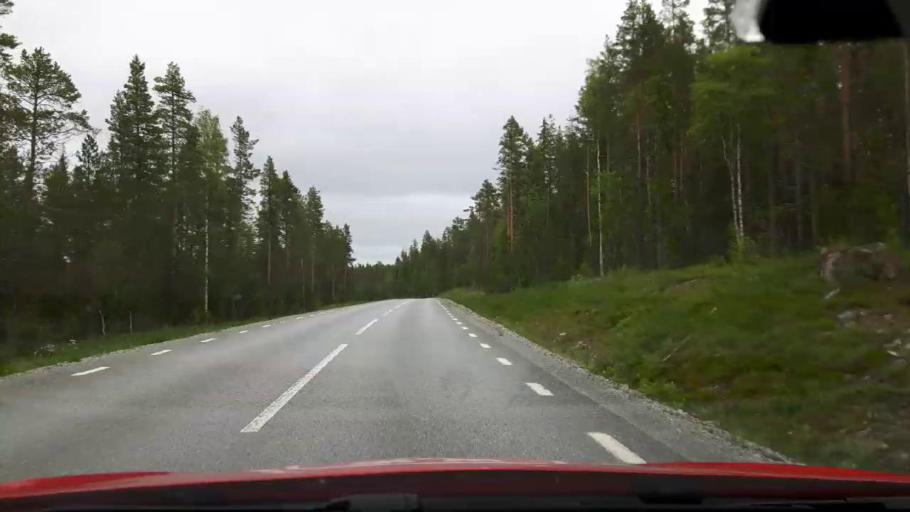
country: SE
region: Jaemtland
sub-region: OEstersunds Kommun
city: Lit
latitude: 63.7128
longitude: 14.7009
